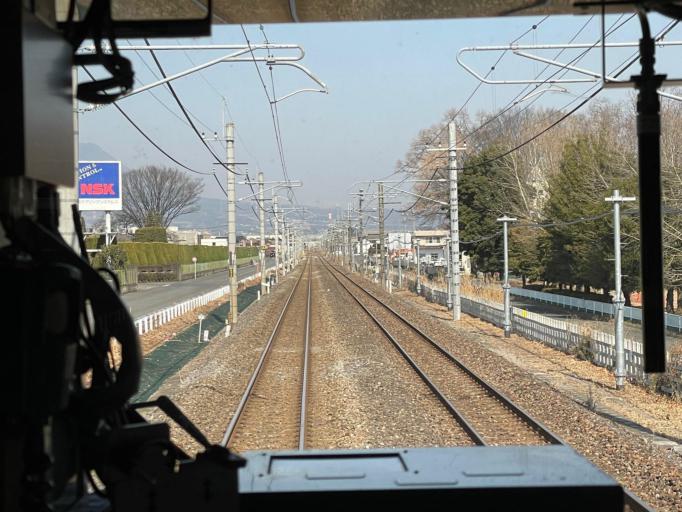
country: JP
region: Gunma
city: Maebashi-shi
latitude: 36.3985
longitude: 139.0453
